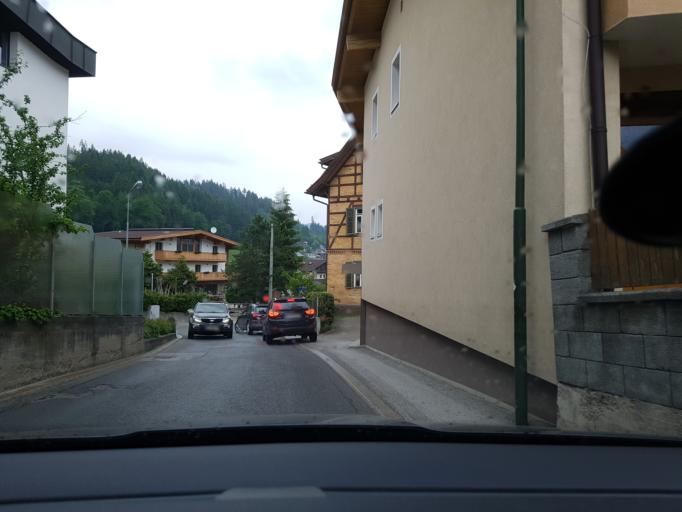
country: AT
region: Tyrol
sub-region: Politischer Bezirk Schwaz
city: Fugen
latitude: 47.3444
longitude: 11.8472
